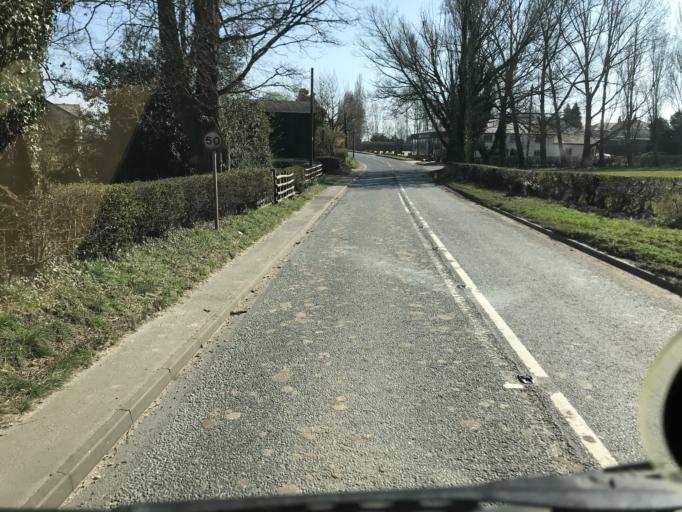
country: GB
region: England
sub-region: Cheshire East
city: Mobberley
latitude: 53.2849
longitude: -2.3302
